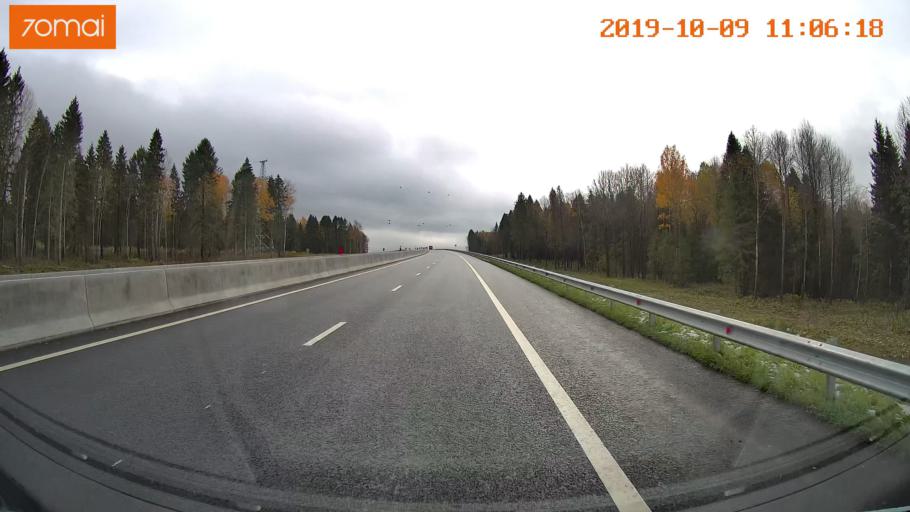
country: RU
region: Vologda
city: Vologda
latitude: 59.1883
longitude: 39.7596
